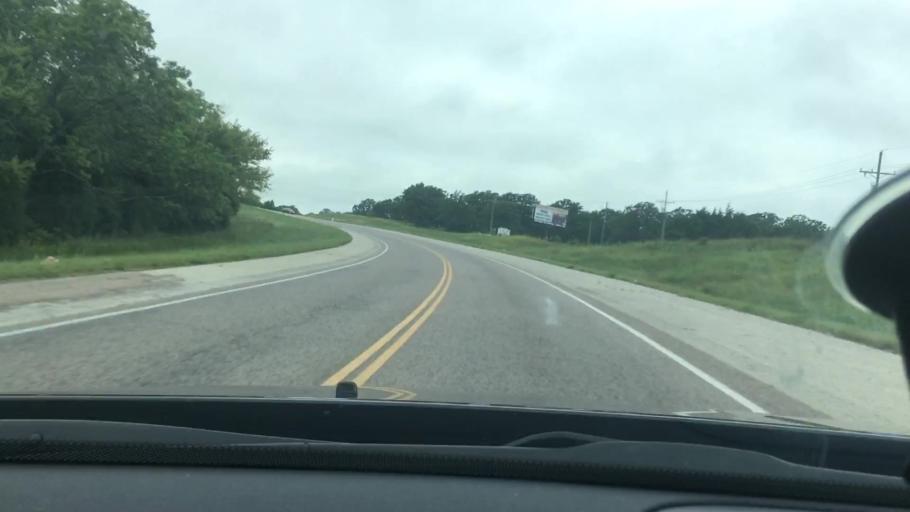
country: US
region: Oklahoma
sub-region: Pontotoc County
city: Ada
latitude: 34.7865
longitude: -96.5715
